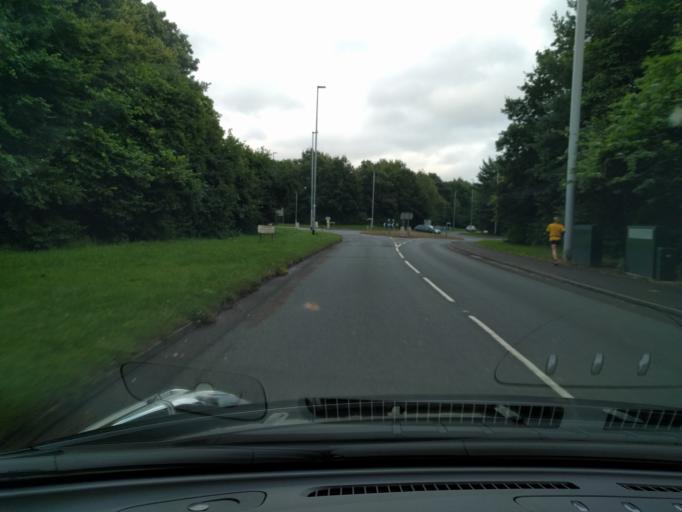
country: GB
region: England
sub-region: Warrington
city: Culcheth
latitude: 53.4277
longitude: -2.5096
